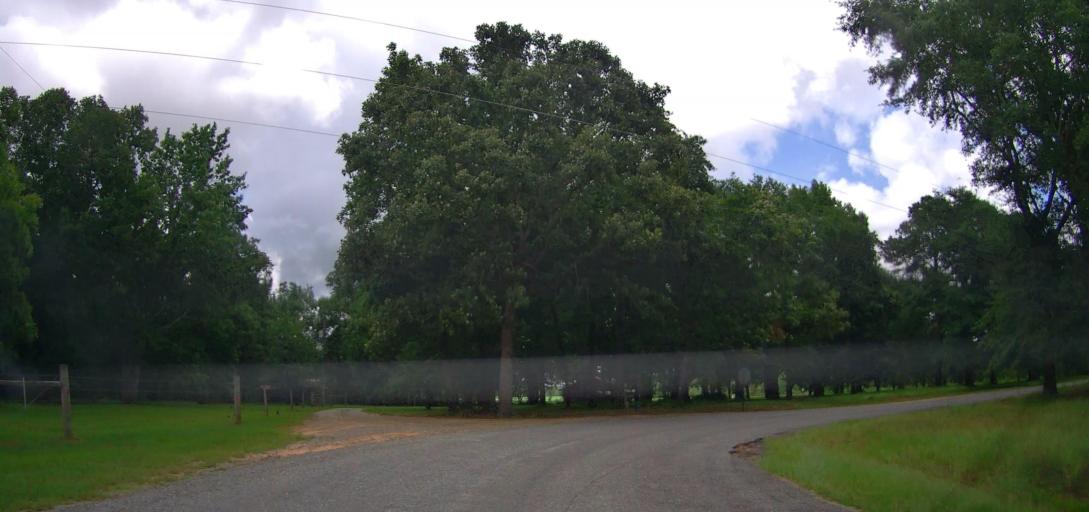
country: US
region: Georgia
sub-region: Pulaski County
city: Hawkinsville
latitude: 32.3181
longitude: -83.5327
